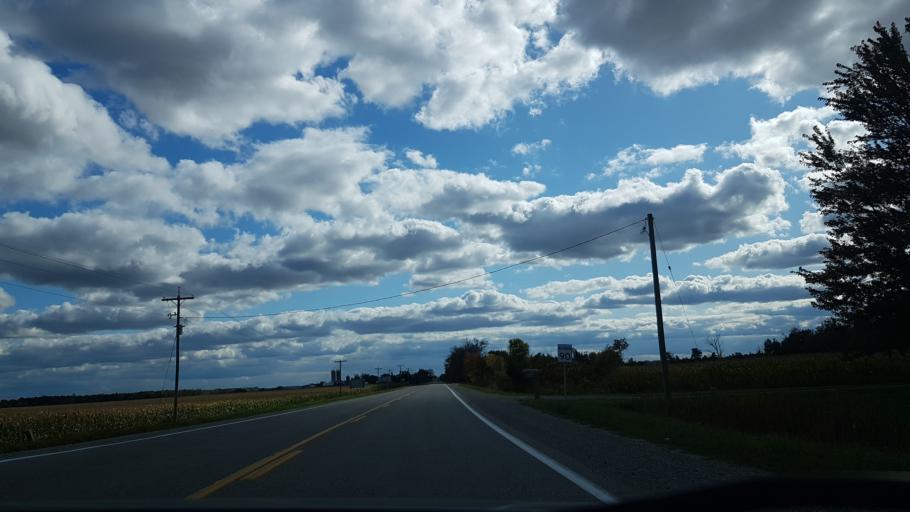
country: CA
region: Ontario
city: South Huron
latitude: 43.2427
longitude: -81.6908
